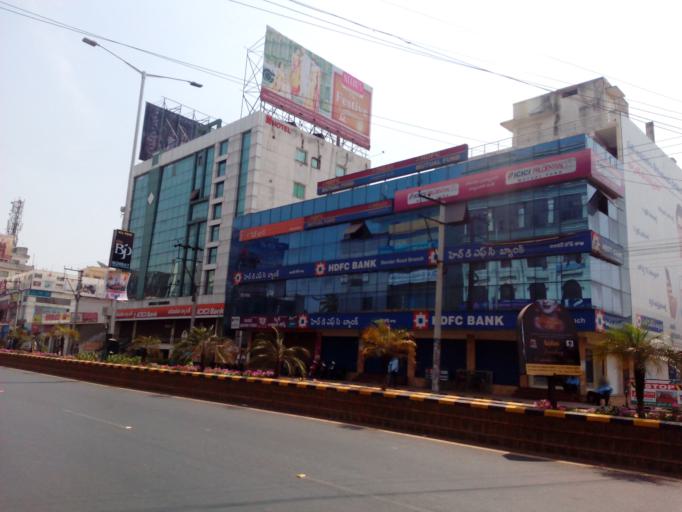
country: IN
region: Andhra Pradesh
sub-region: Krishna
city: Yanamalakuduru
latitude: 16.4988
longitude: 80.6518
